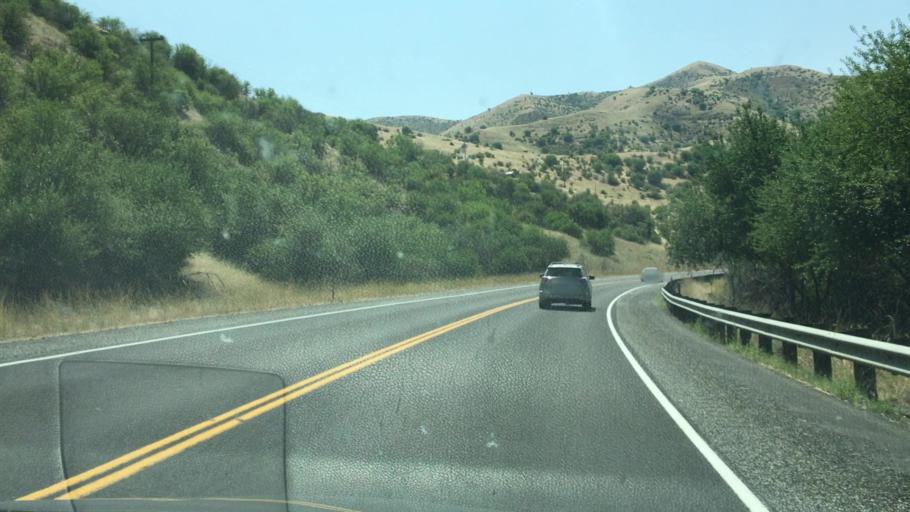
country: US
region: Idaho
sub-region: Idaho County
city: Grangeville
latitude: 45.7277
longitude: -116.3012
